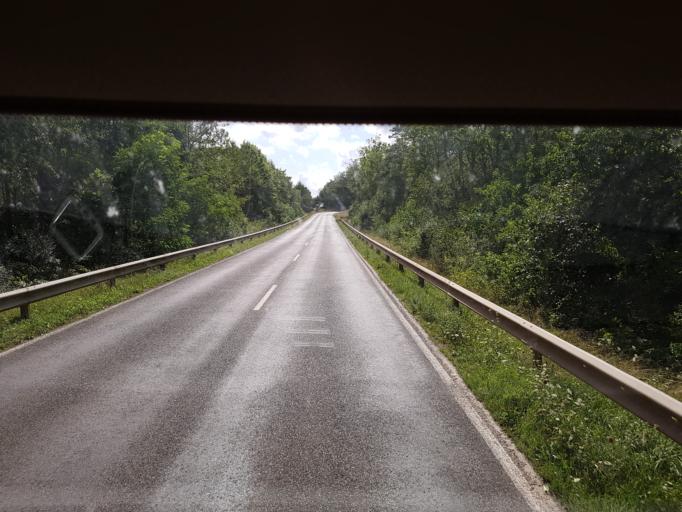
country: DE
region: Rheinland-Pfalz
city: Hetzerath
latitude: 49.8706
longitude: 6.8035
